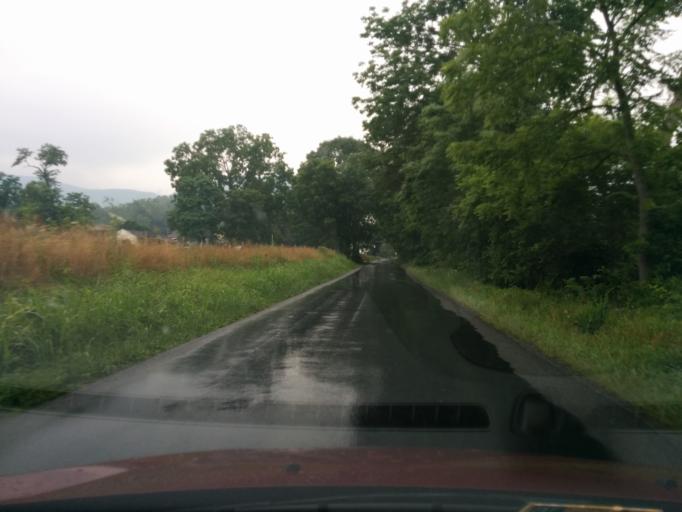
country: US
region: Virginia
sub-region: Rockbridge County
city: East Lexington
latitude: 37.9032
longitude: -79.4167
